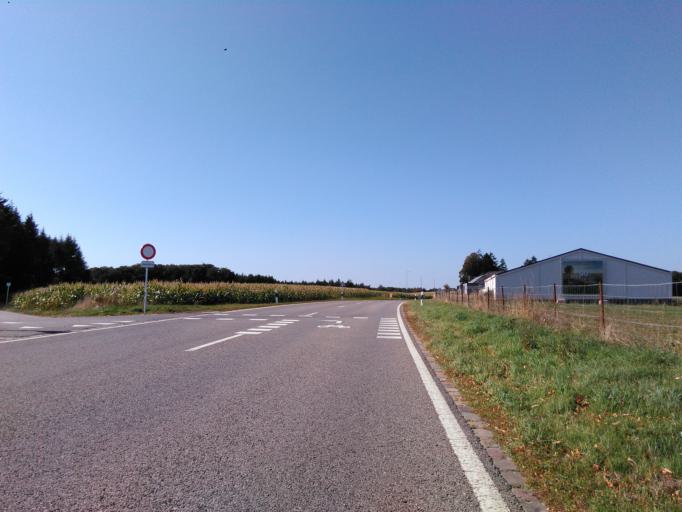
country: LU
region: Diekirch
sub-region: Canton de Redange
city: Rambrouch
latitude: 49.8391
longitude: 5.8286
